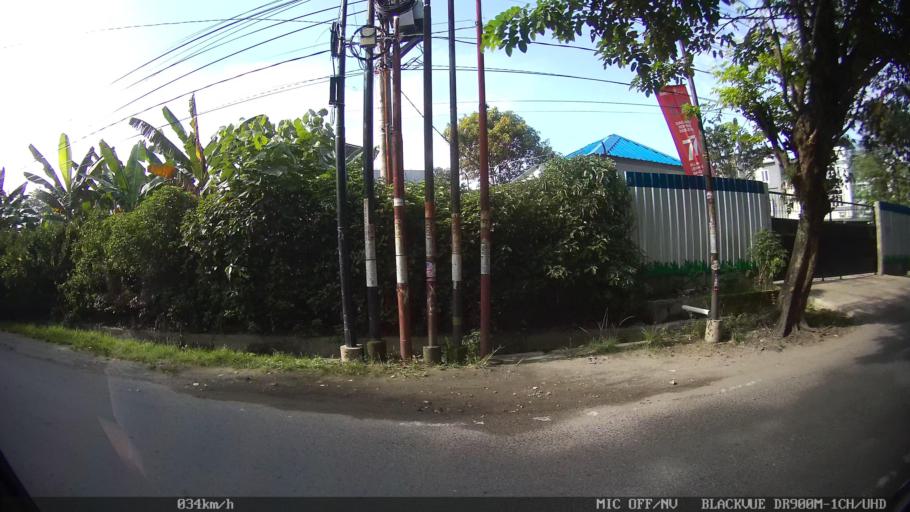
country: ID
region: North Sumatra
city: Medan
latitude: 3.6040
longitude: 98.6577
